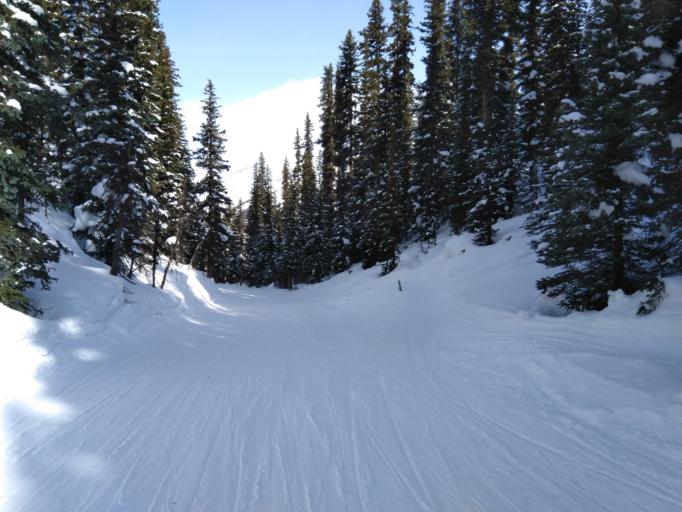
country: CA
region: Alberta
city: Banff
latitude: 51.0923
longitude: -115.7701
